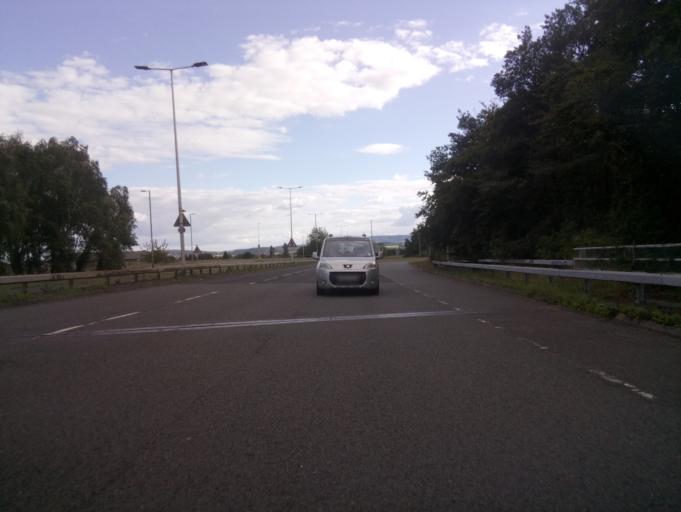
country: GB
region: England
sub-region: Devon
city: Heavitree
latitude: 50.7069
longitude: -3.4858
